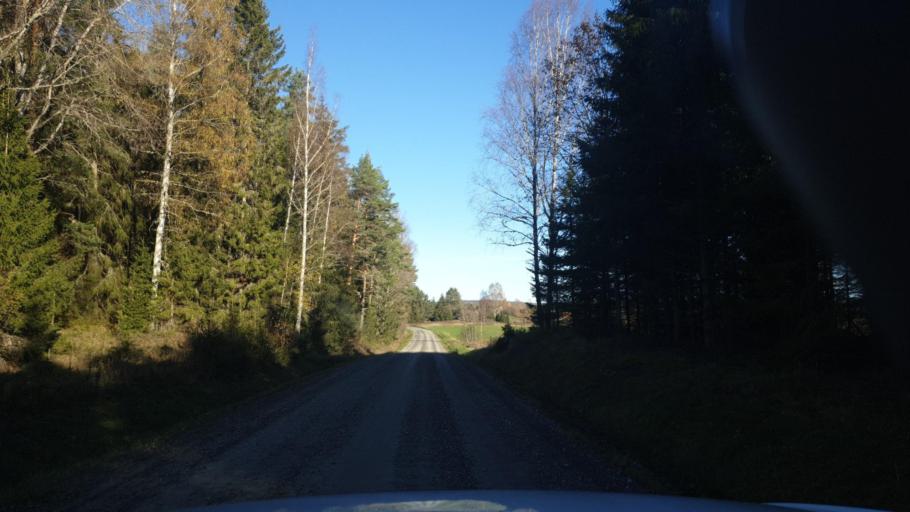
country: SE
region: Vaermland
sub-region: Karlstads Kommun
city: Edsvalla
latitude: 59.5449
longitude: 13.0062
